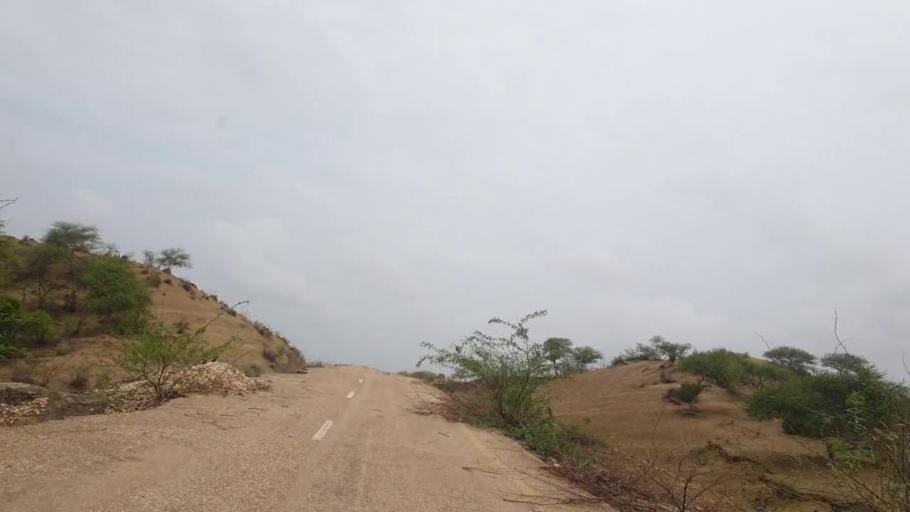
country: PK
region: Sindh
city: Naukot
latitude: 24.6314
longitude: 69.3547
